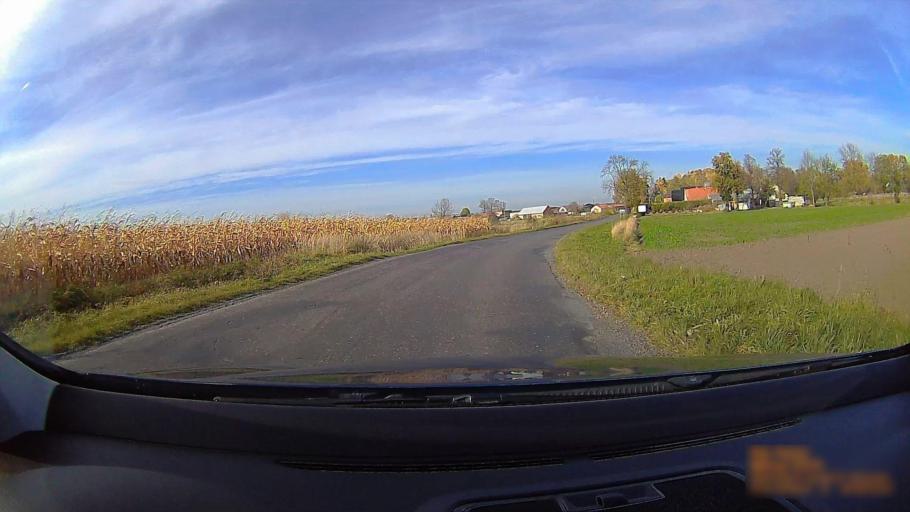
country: PL
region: Greater Poland Voivodeship
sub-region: Powiat ostrzeszowski
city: Doruchow
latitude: 51.4252
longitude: 18.0536
